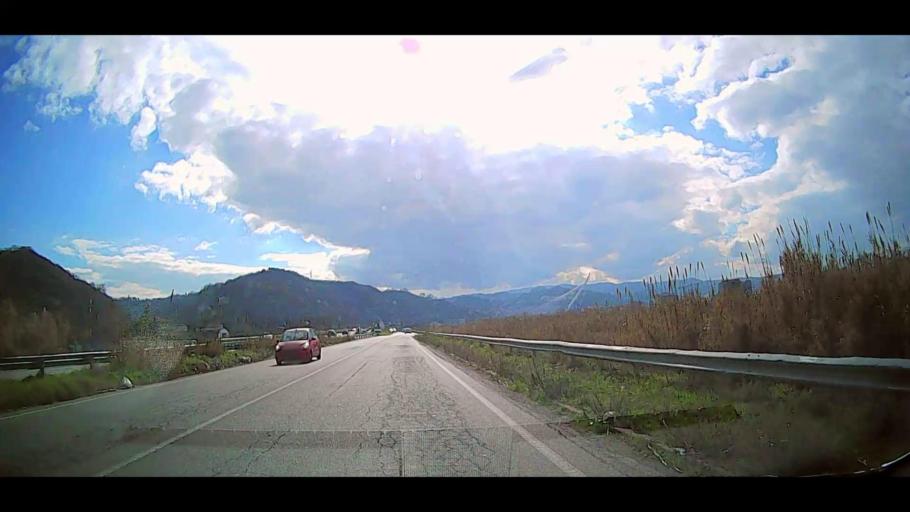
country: IT
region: Calabria
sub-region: Provincia di Cosenza
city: Cosenza
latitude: 39.3081
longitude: 16.2626
